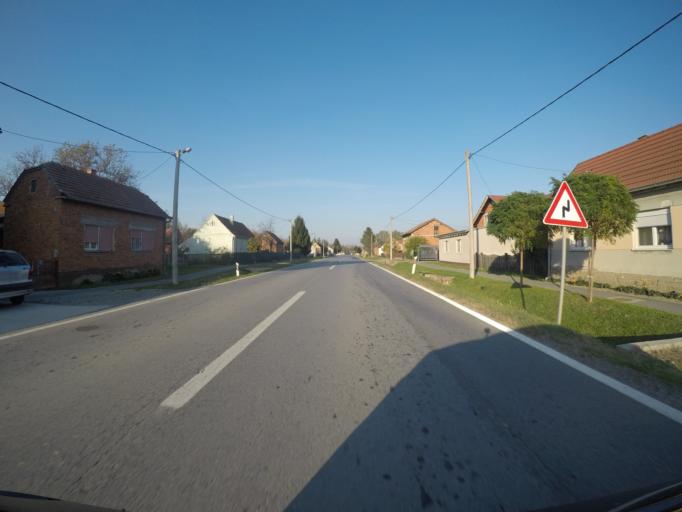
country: HU
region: Somogy
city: Barcs
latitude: 45.8980
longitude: 17.4352
